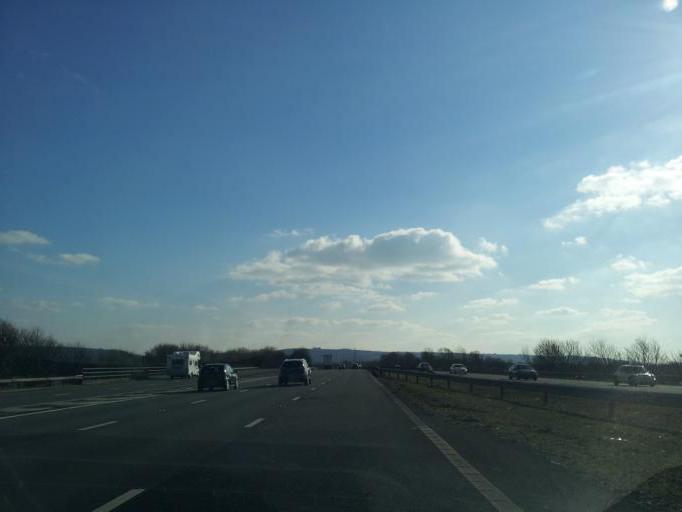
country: GB
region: England
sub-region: North Somerset
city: St. Georges
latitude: 51.3662
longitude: -2.8906
